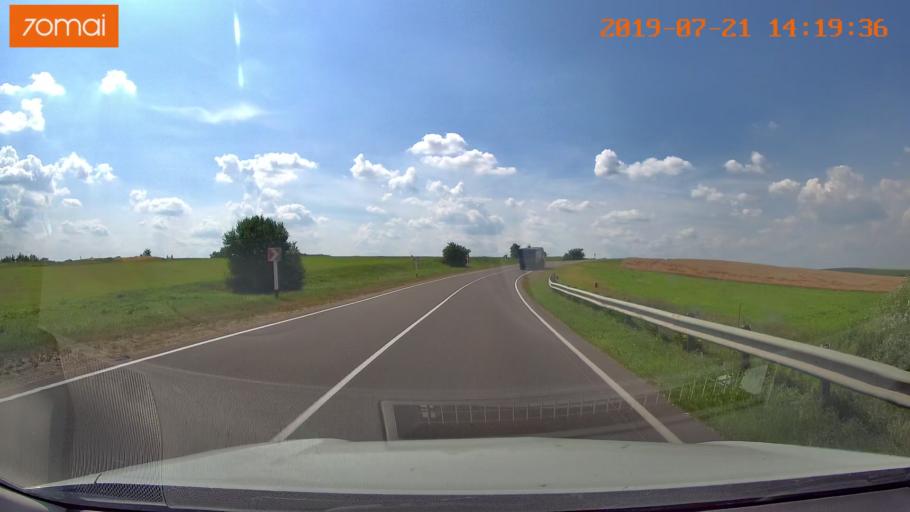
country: BY
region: Grodnenskaya
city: Karelichy
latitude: 53.5868
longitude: 26.1691
